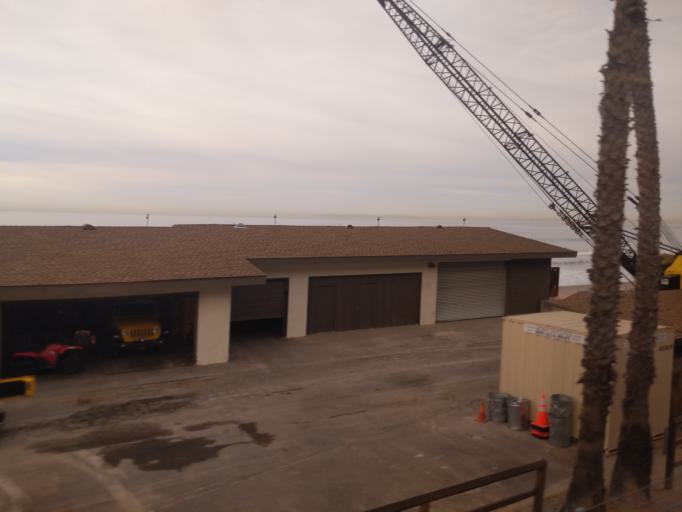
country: US
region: California
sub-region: Orange County
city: San Clemente
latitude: 33.4212
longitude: -117.6211
